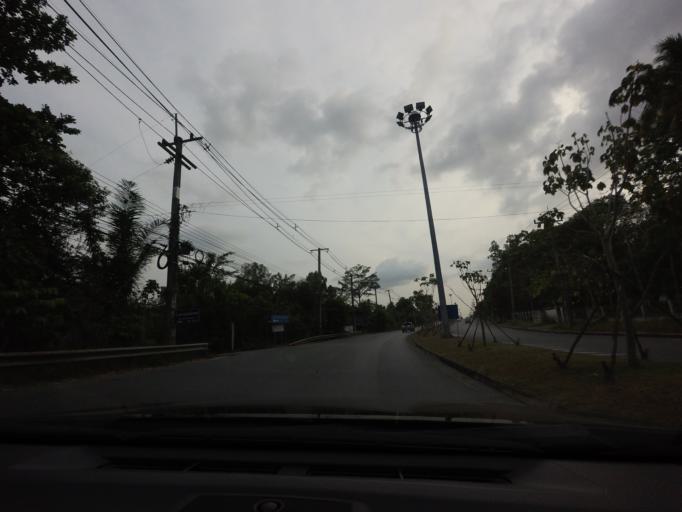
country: TH
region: Yala
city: Yala
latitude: 6.5225
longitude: 101.2820
